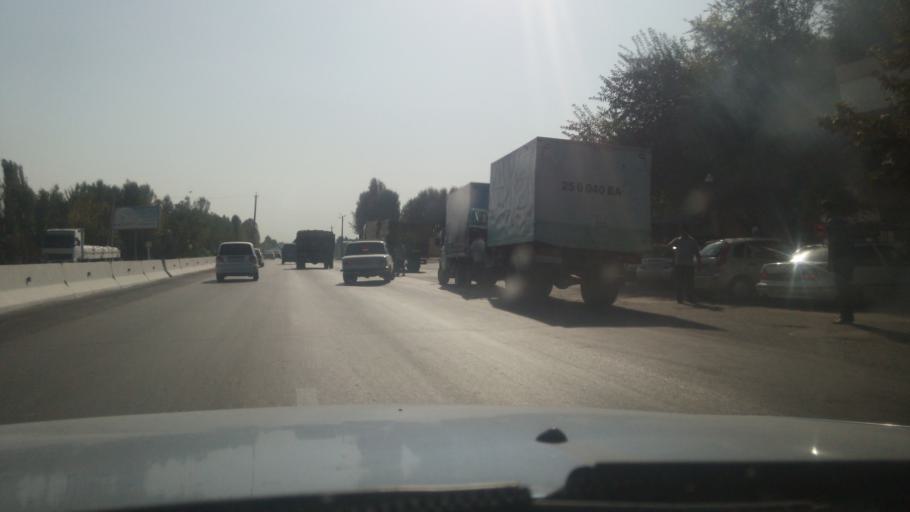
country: UZ
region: Toshkent
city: Urtaowul
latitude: 41.2181
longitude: 69.1324
